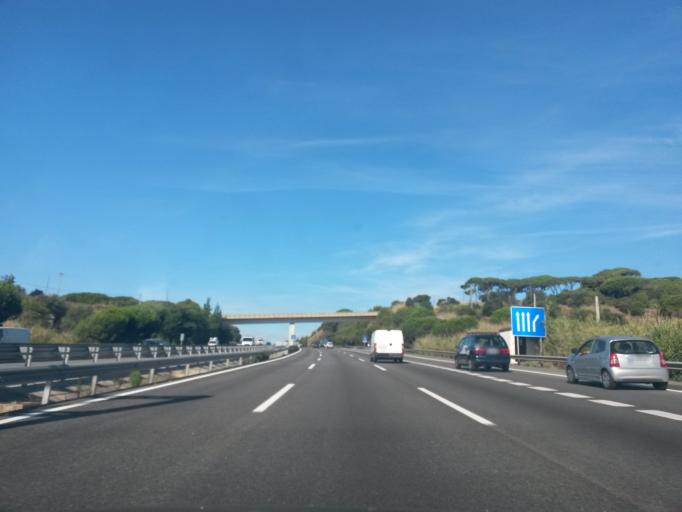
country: ES
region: Catalonia
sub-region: Provincia de Barcelona
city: Sant Andreu de Llavaneres
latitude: 41.5594
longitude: 2.4668
